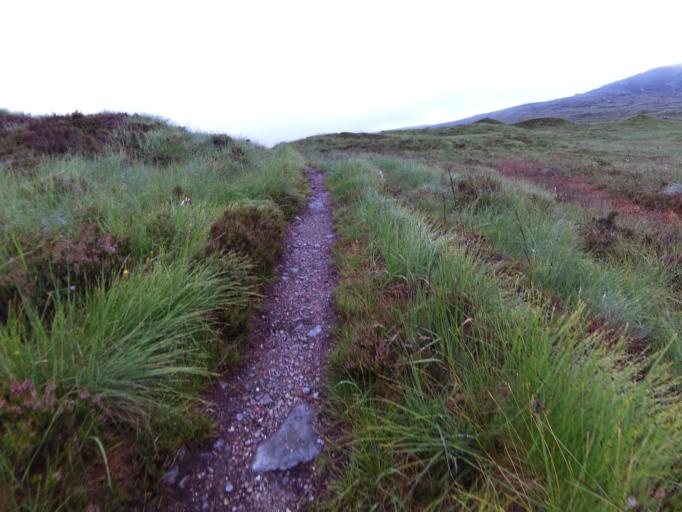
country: GB
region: Scotland
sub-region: Highland
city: Spean Bridge
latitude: 56.7657
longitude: -4.7016
